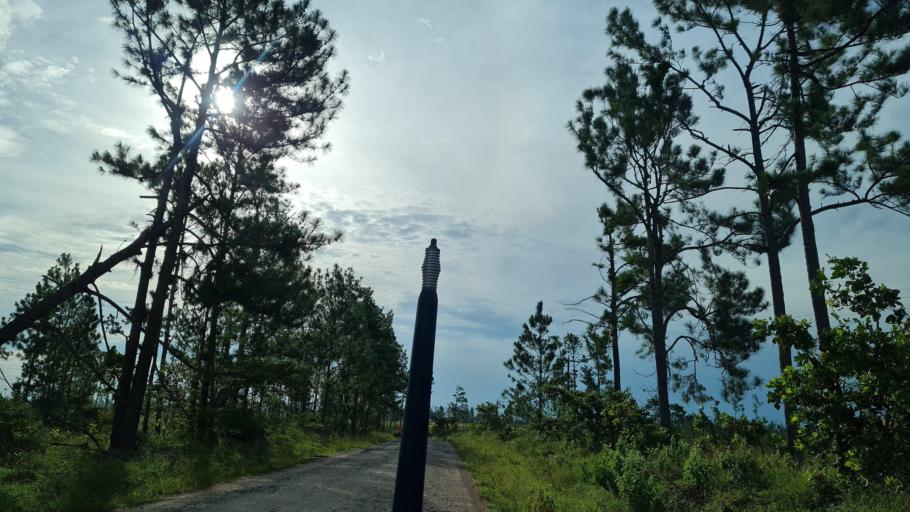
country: NI
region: Atlantico Sur
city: La Cruz de Rio Grande
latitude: 13.5264
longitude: -84.2520
